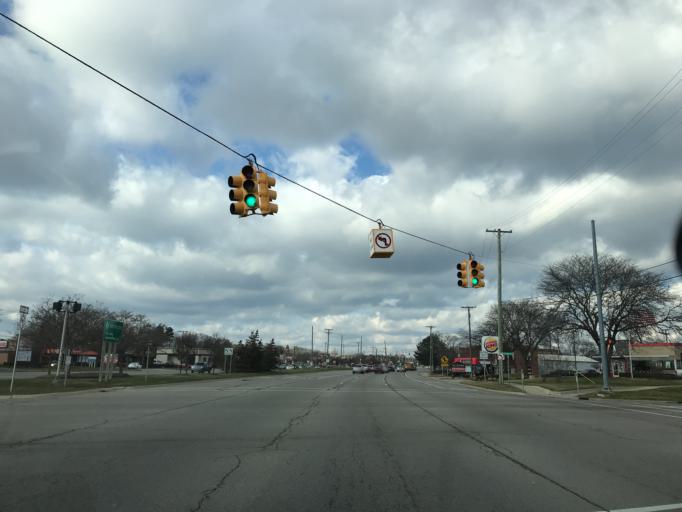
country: US
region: Michigan
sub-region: Oakland County
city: Franklin
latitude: 42.4990
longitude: -83.3043
